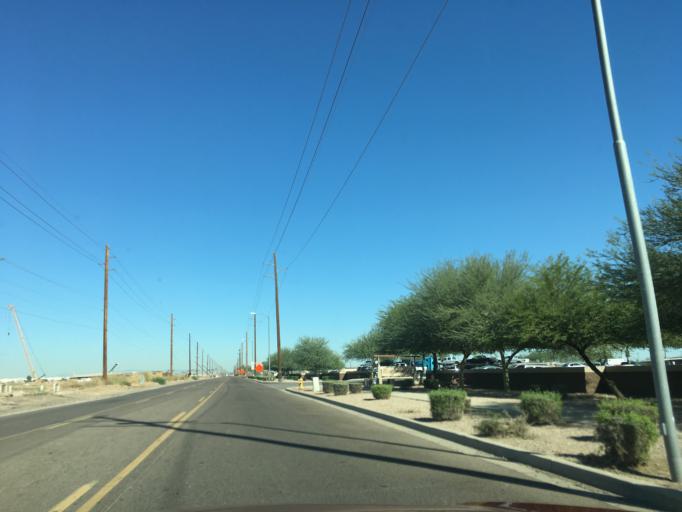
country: US
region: Arizona
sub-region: Maricopa County
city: Laveen
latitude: 33.4255
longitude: -112.1865
